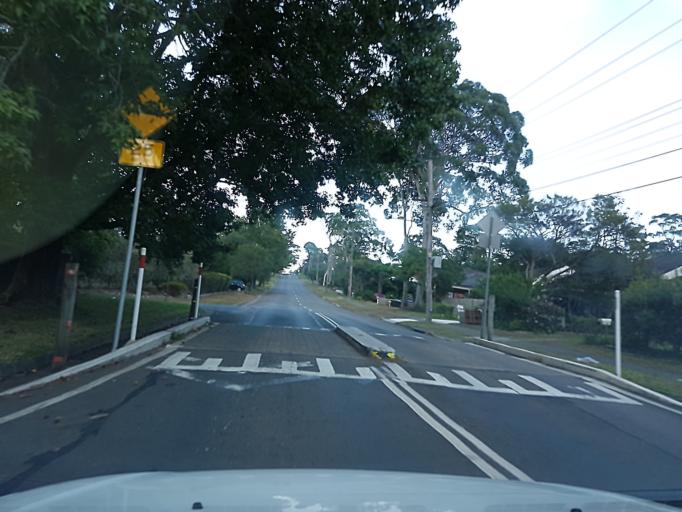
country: AU
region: New South Wales
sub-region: Warringah
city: Davidson
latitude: -33.7463
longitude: 151.2263
